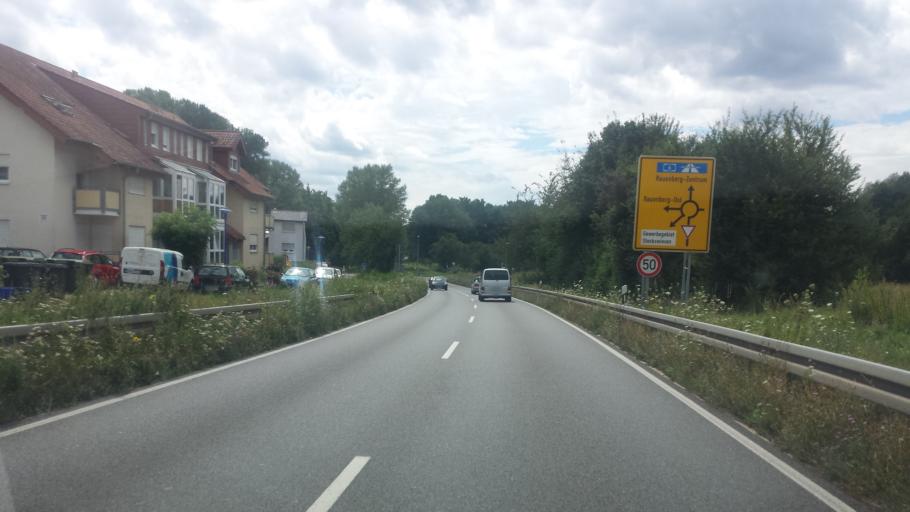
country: DE
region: Baden-Wuerttemberg
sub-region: Karlsruhe Region
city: Rauenberg
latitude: 49.2776
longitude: 8.7077
